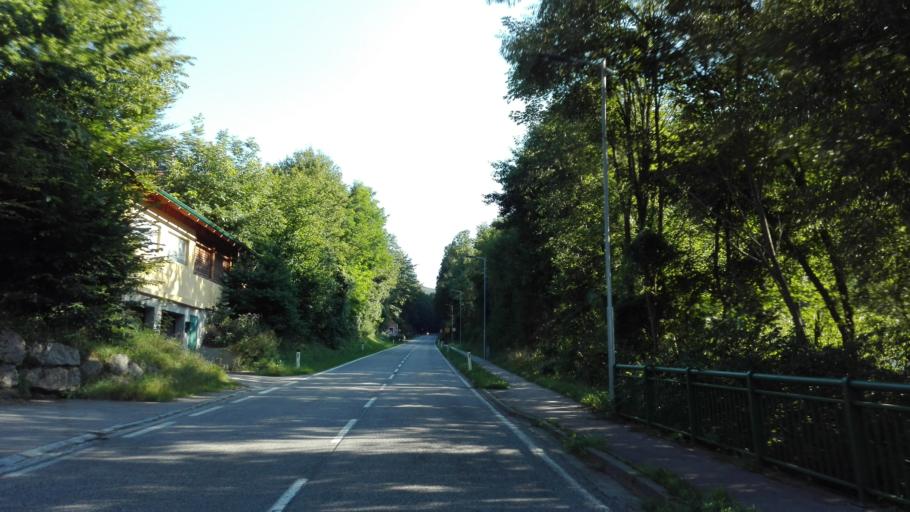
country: AT
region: Lower Austria
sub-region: Politischer Bezirk Sankt Polten
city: Stossing
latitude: 48.0855
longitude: 15.8650
